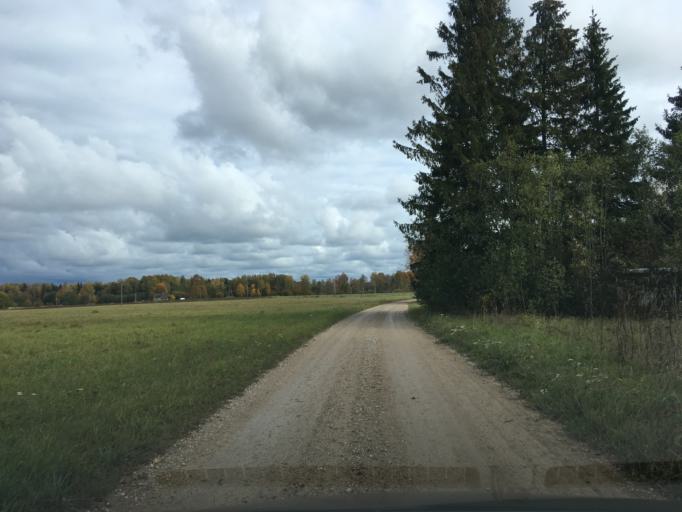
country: EE
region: Harju
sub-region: Raasiku vald
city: Raasiku
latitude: 59.2151
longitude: 25.2127
